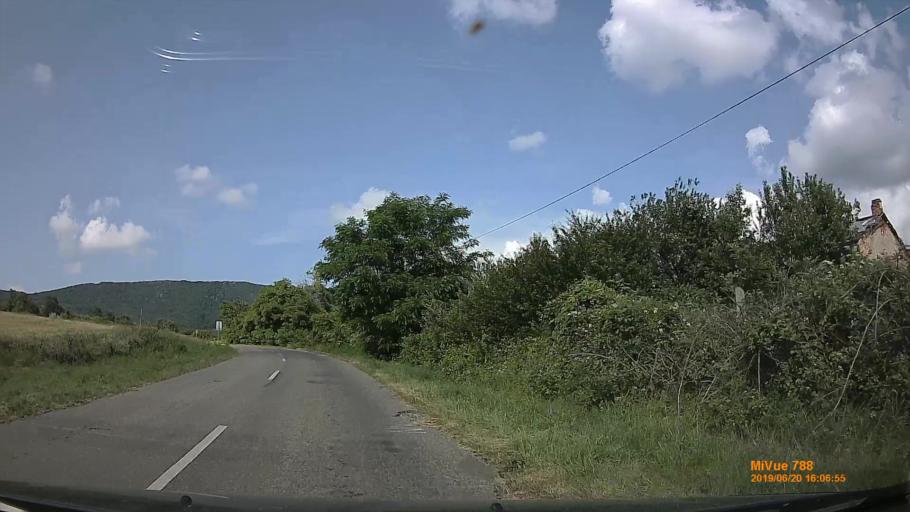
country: HU
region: Baranya
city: Pellerd
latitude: 46.0834
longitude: 18.1115
